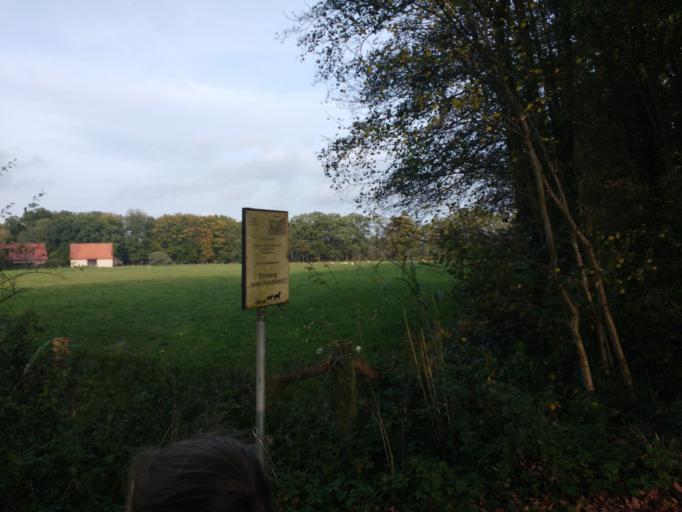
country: DE
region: North Rhine-Westphalia
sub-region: Regierungsbezirk Detmold
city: Delbruck
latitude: 51.7762
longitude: 8.6136
